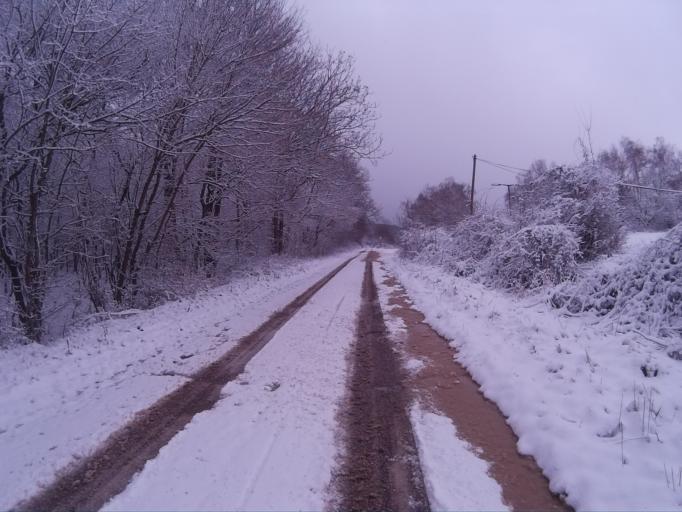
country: HU
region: Komarom-Esztergom
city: Tarjan
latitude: 47.5732
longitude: 18.5041
